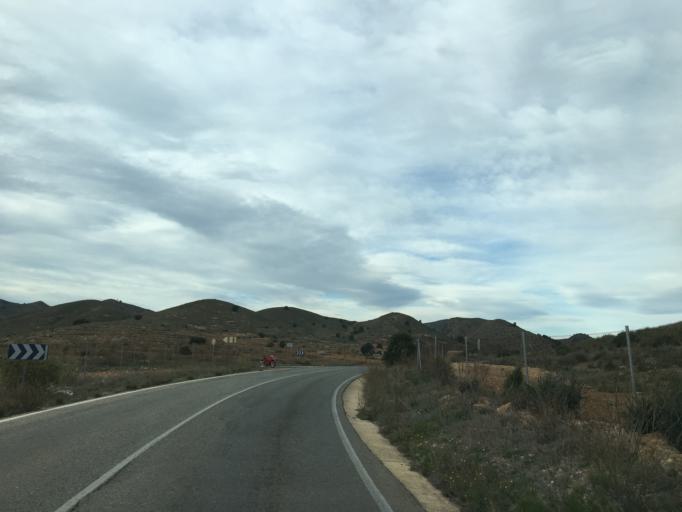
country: ES
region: Murcia
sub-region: Murcia
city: Fuente-Alamo de Murcia
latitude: 37.6129
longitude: -1.0987
